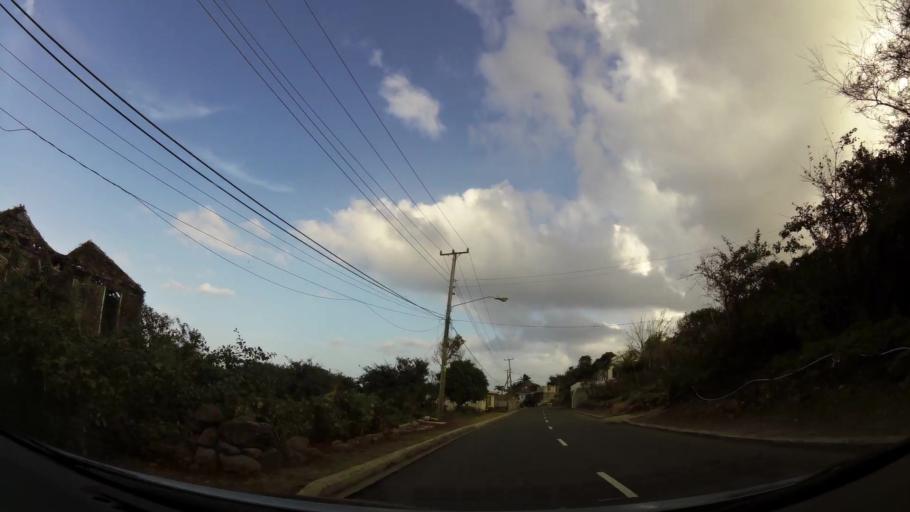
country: KN
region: Saint James Windwa
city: Newcastle
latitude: 17.1959
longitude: -62.5720
